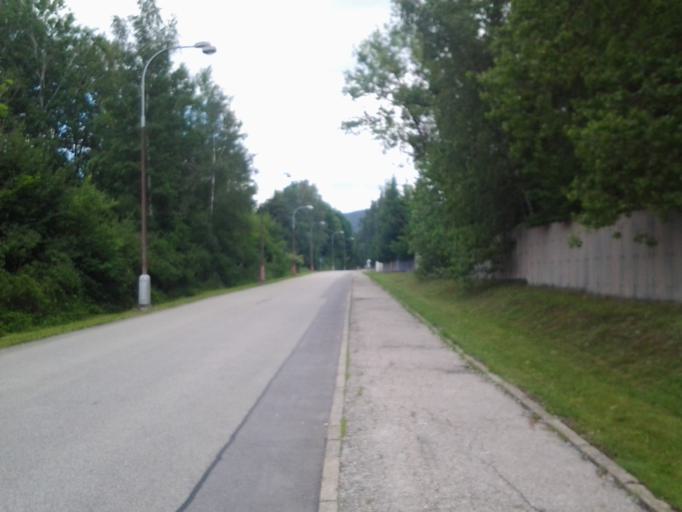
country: CZ
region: Jihocesky
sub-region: Okres Cesky Krumlov
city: Cesky Krumlov
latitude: 48.8249
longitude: 14.3086
